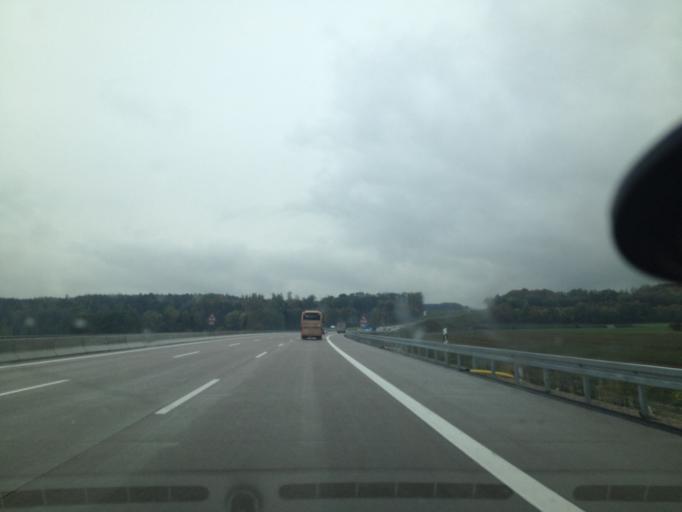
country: DE
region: Bavaria
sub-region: Swabia
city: Burgau
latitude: 48.4126
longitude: 10.4191
